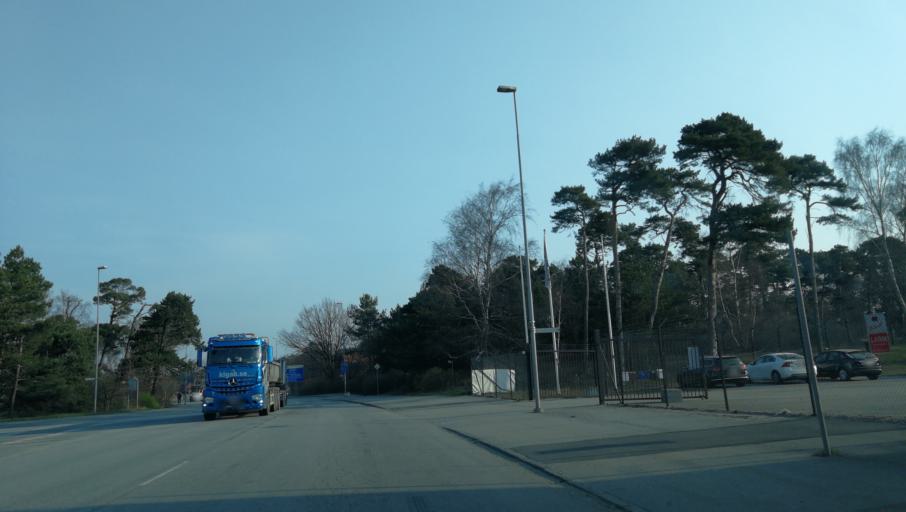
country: SE
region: Skane
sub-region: Ystads Kommun
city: Ystad
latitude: 55.4273
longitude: 13.8409
